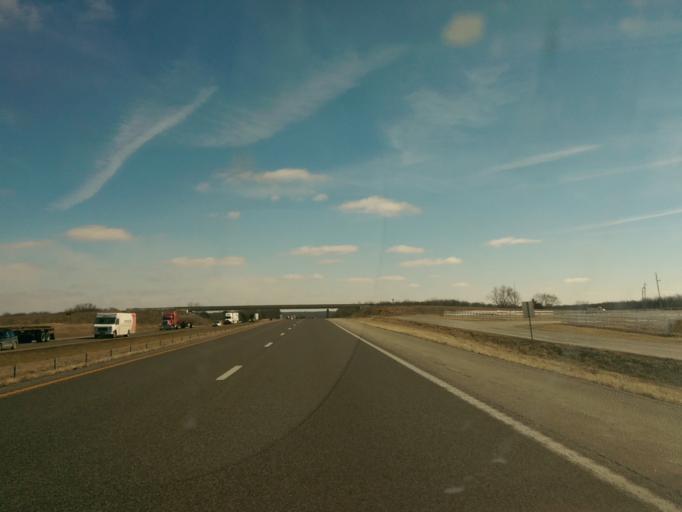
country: US
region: Missouri
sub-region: Callaway County
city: Fulton
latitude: 38.9403
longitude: -91.8684
